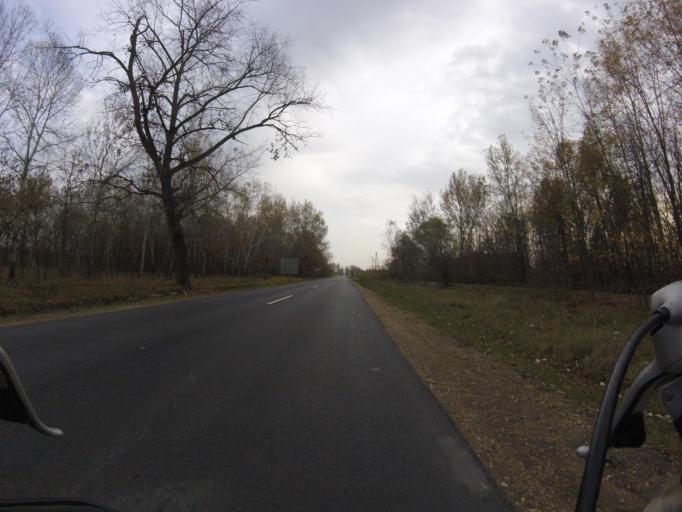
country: HU
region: Pest
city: Csemo
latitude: 47.1017
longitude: 19.6302
